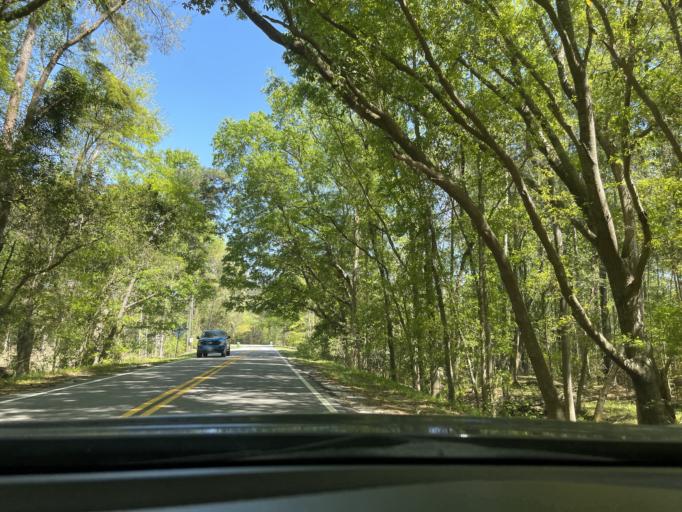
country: US
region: Georgia
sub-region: Chatham County
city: Pooler
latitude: 32.0904
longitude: -81.2445
